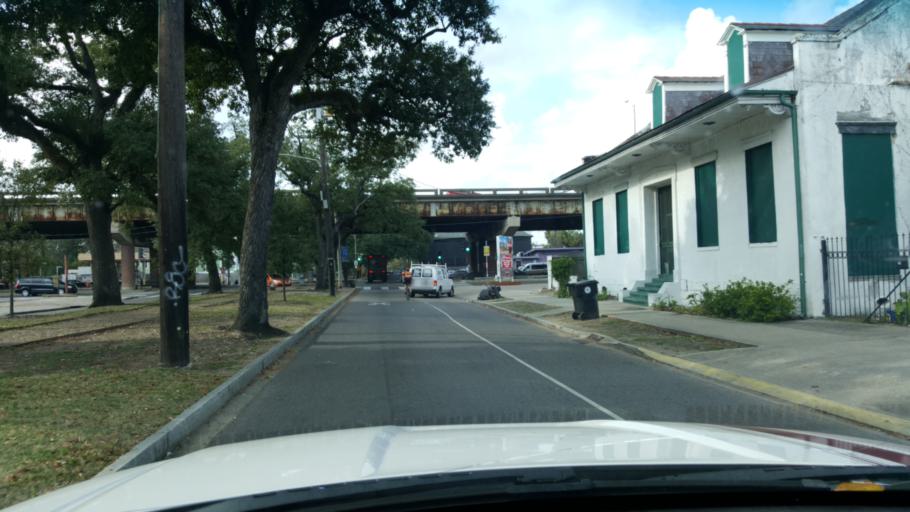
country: US
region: Louisiana
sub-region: Orleans Parish
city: New Orleans
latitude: 29.9689
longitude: -90.0678
